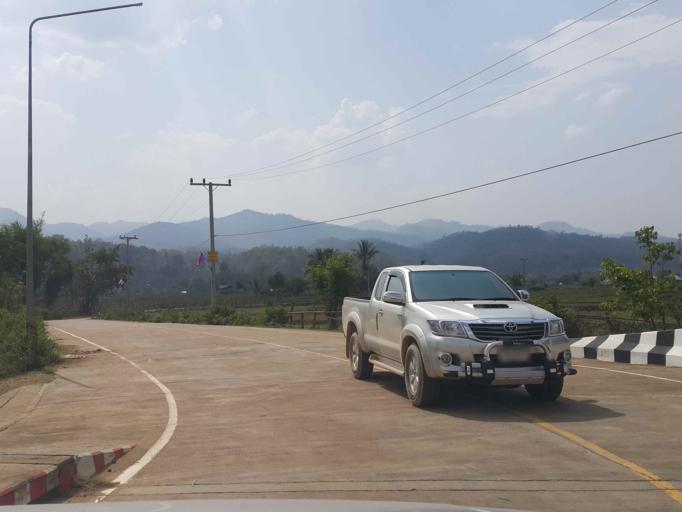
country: TH
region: Chiang Mai
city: Wiang Haeng
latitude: 19.3788
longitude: 98.7210
